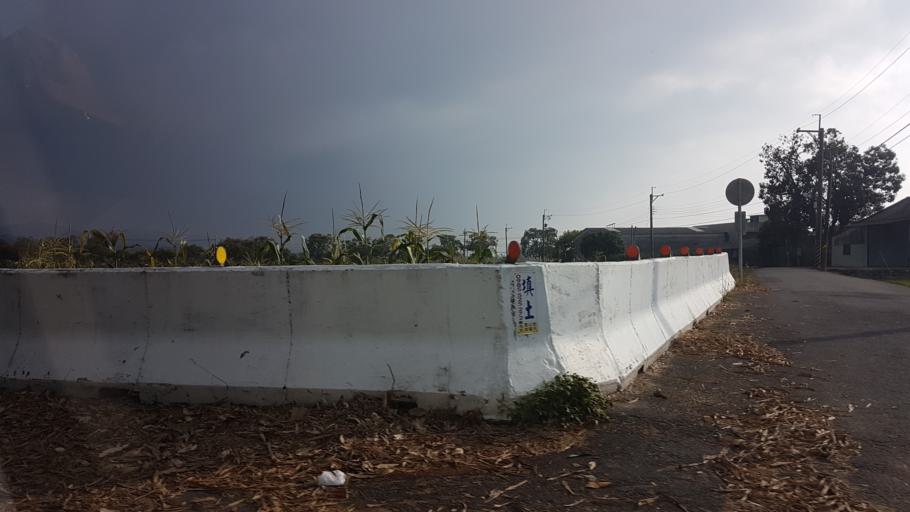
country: TW
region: Taiwan
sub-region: Chiayi
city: Jiayi Shi
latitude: 23.3782
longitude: 120.4397
